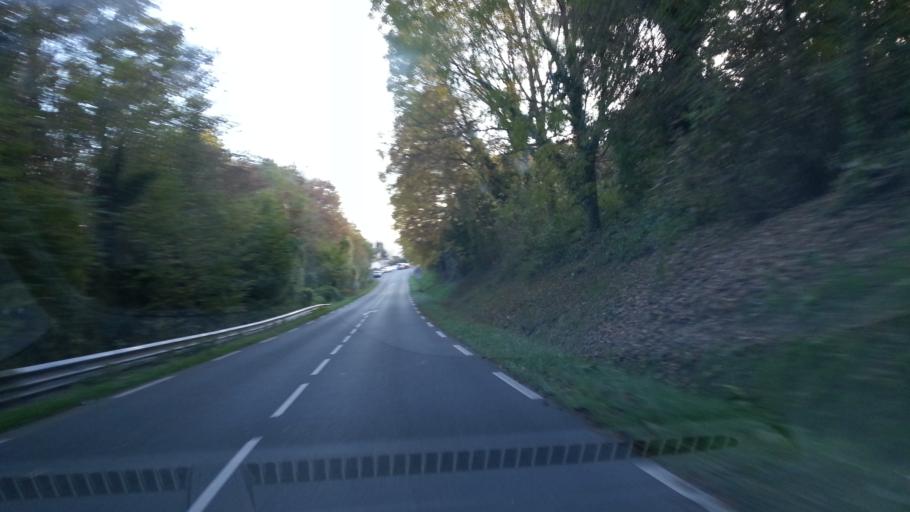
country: FR
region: Picardie
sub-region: Departement de l'Oise
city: Cires-les-Mello
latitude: 49.2838
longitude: 2.3612
